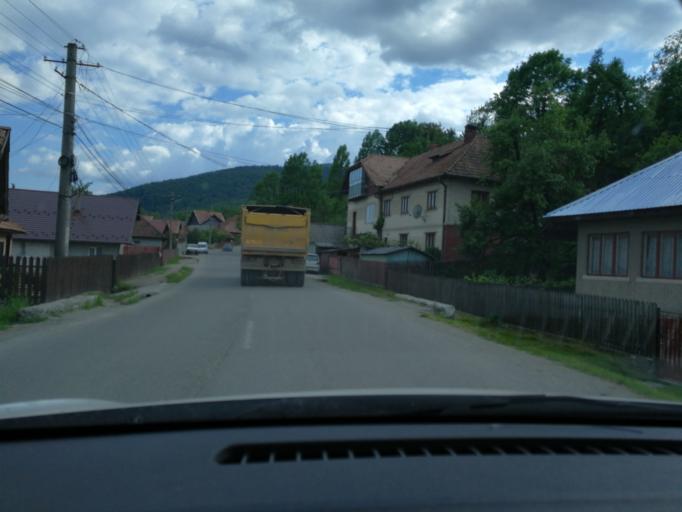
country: RO
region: Prahova
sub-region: Comuna Valea Doftanei
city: Tesila
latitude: 45.2989
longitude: 25.7205
